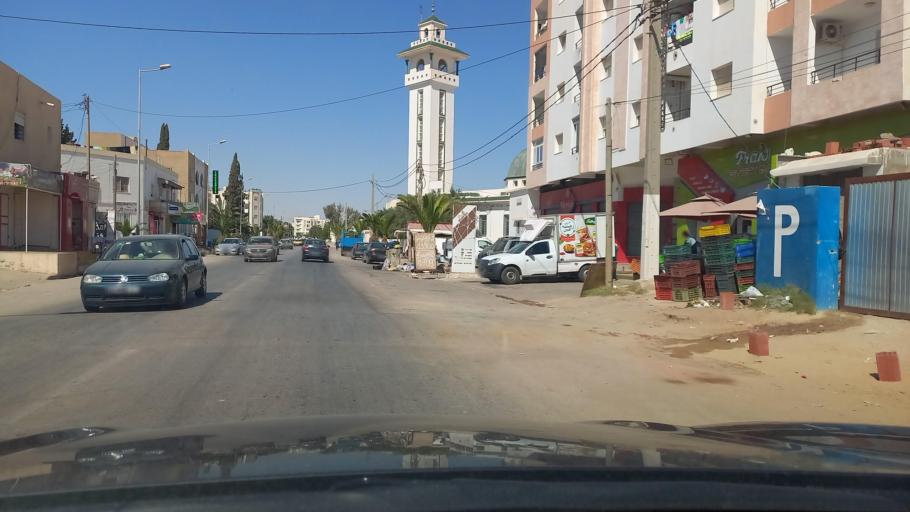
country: TN
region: Safaqis
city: Sfax
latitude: 34.7295
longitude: 10.7319
